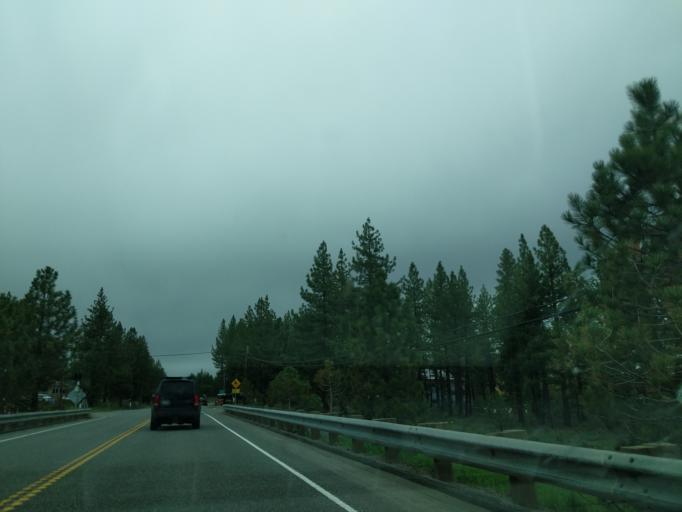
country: US
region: California
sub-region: Nevada County
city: Truckee
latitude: 39.3156
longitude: -120.1508
